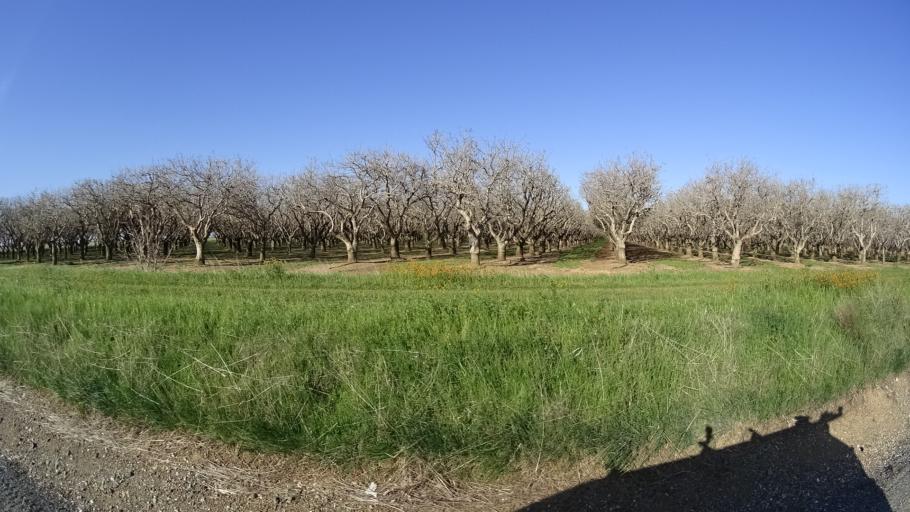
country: US
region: California
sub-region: Glenn County
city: Orland
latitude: 39.7871
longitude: -122.1196
